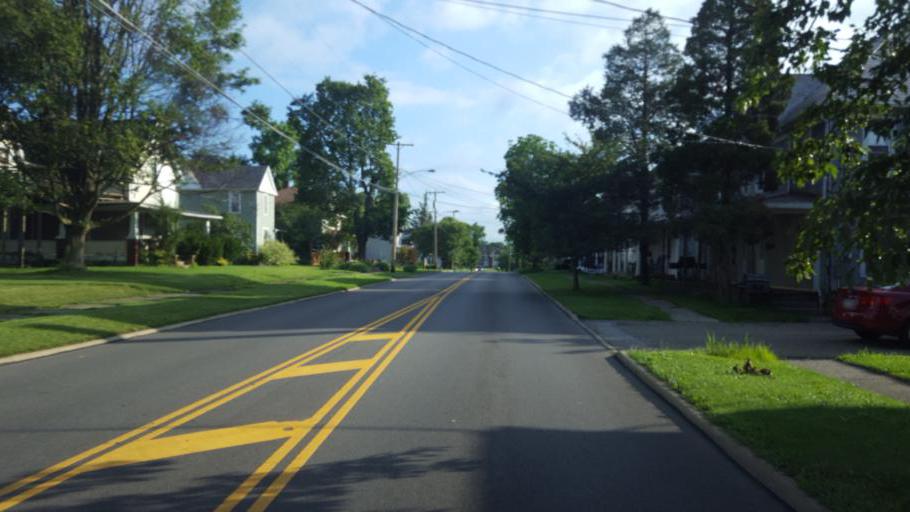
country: US
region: Ohio
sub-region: Richland County
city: Shelby
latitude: 40.8771
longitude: -82.6622
